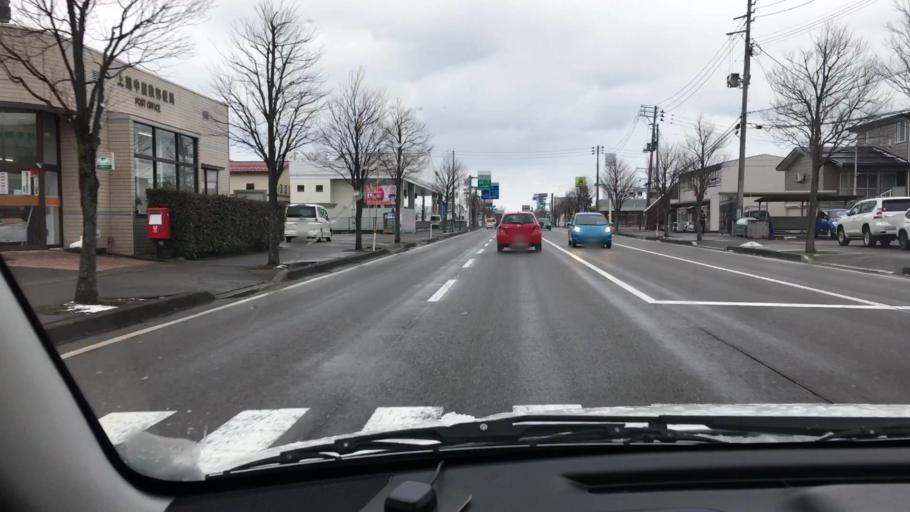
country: JP
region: Niigata
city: Joetsu
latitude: 37.1455
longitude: 138.2284
